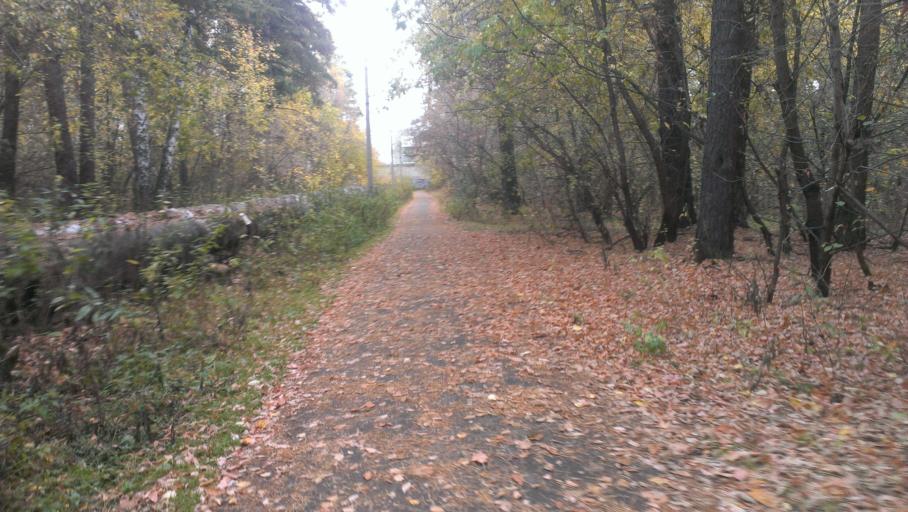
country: RU
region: Altai Krai
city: Yuzhnyy
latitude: 53.2594
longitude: 83.6892
